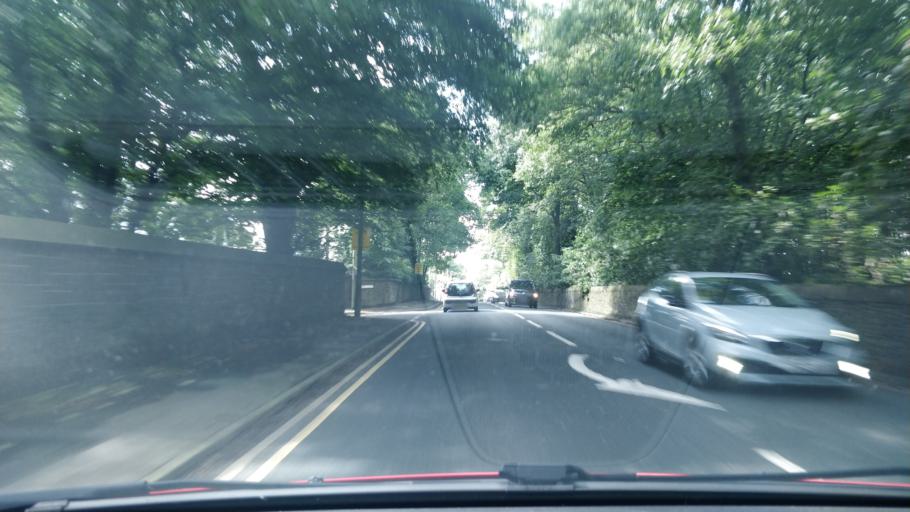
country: GB
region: England
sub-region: Lancashire
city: Appley Bridge
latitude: 53.5917
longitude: -2.7091
